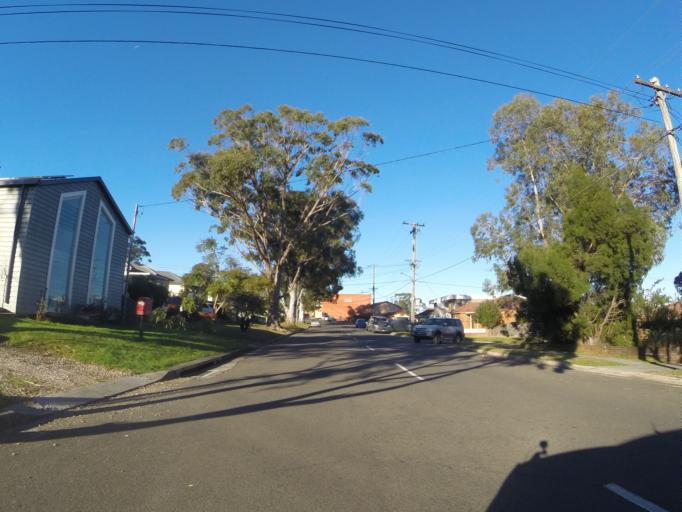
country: AU
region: New South Wales
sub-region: Sutherland Shire
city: Loftus
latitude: -34.0413
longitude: 151.0494
